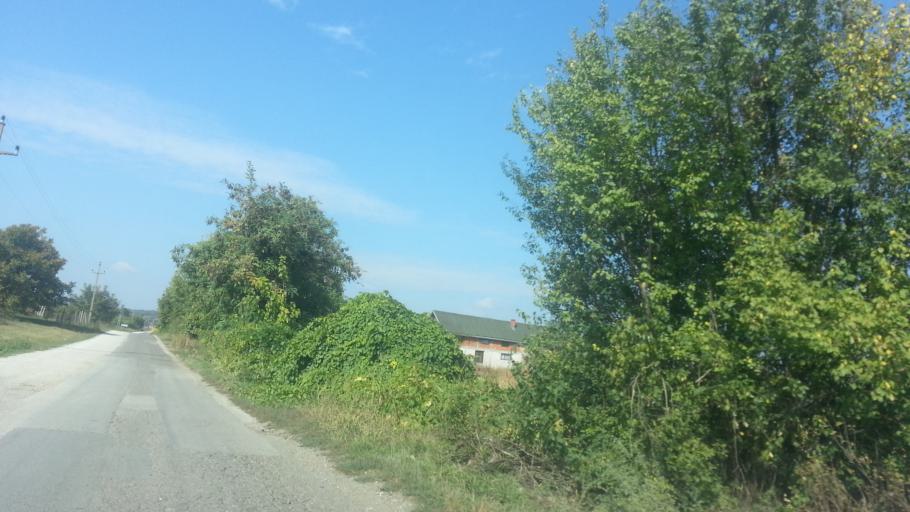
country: RS
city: Novi Slankamen
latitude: 45.1259
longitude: 20.2609
